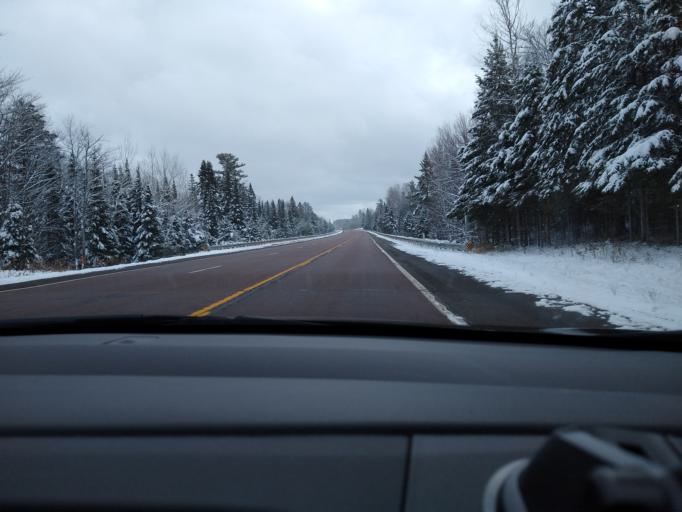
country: US
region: Wisconsin
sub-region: Vilas County
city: Eagle River
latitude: 46.1987
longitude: -89.0091
